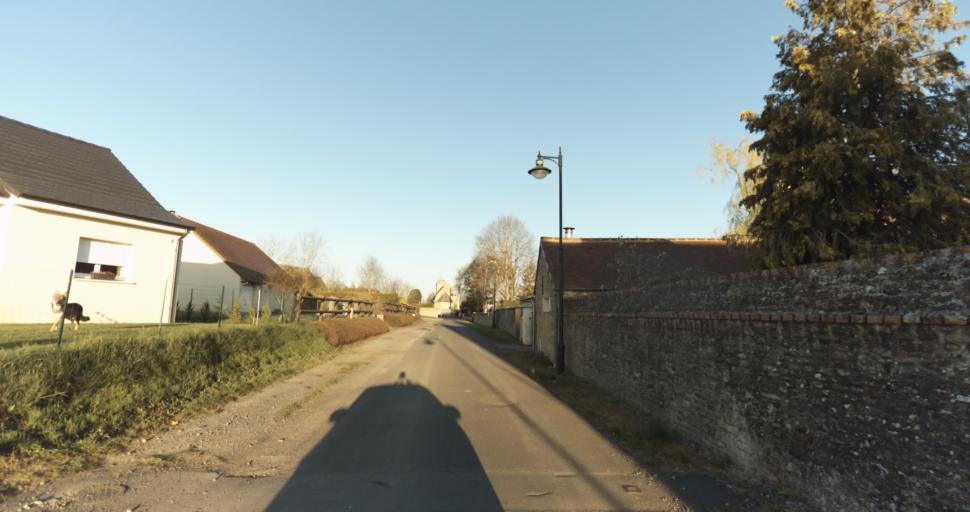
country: FR
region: Lower Normandy
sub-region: Departement du Calvados
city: Saint-Pierre-sur-Dives
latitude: 49.0237
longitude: -0.0134
